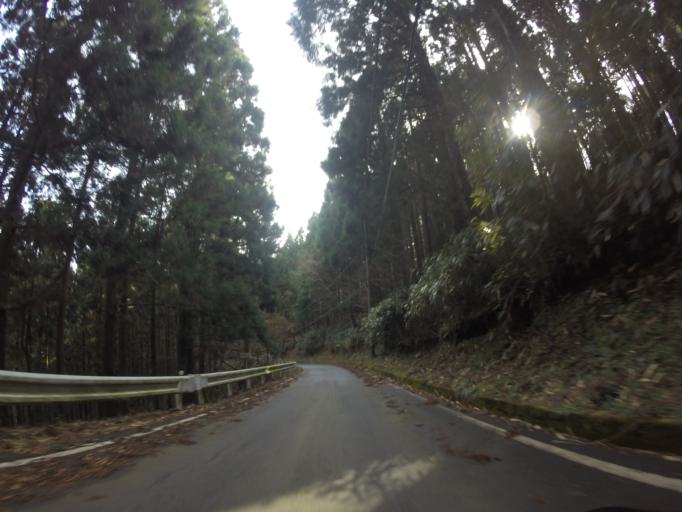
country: JP
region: Shizuoka
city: Heda
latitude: 34.8741
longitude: 138.8546
